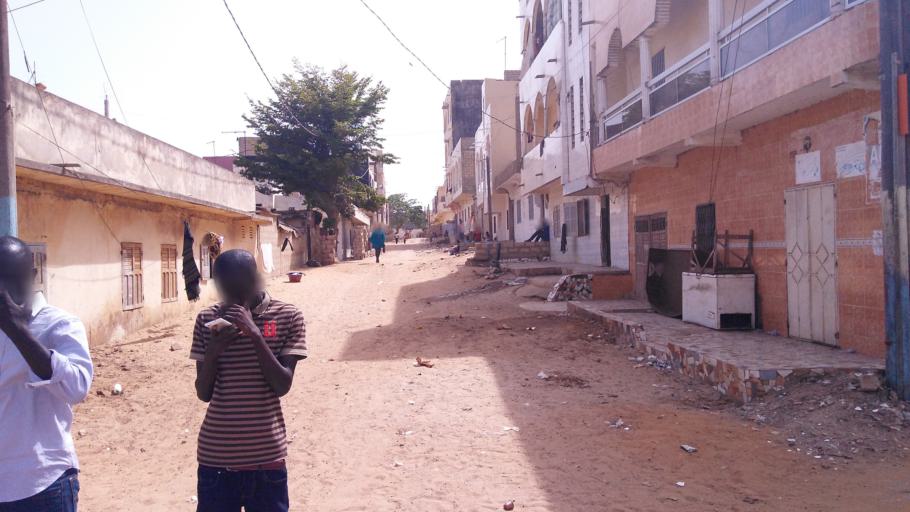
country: SN
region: Dakar
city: Pikine
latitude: 14.7794
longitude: -17.3775
